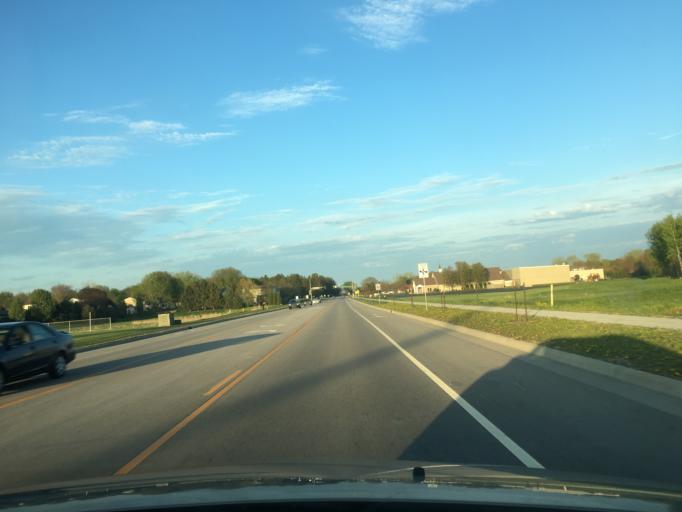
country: US
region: Minnesota
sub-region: Olmsted County
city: Rochester
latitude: 44.0794
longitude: -92.5326
